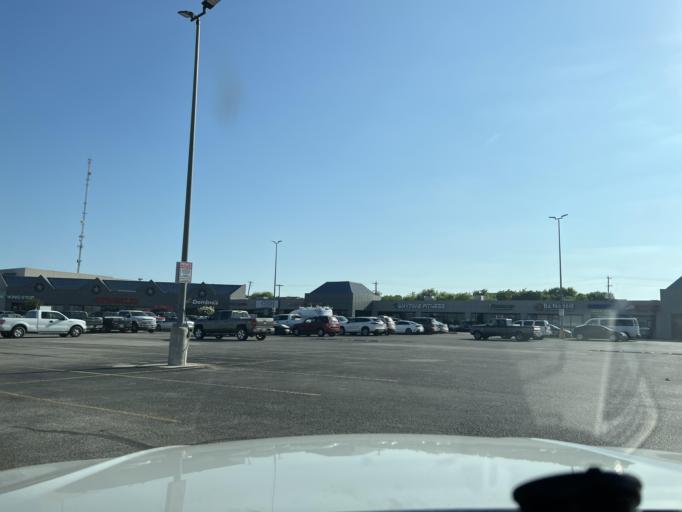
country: US
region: Texas
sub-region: Washington County
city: Brenham
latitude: 30.1413
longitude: -96.3972
